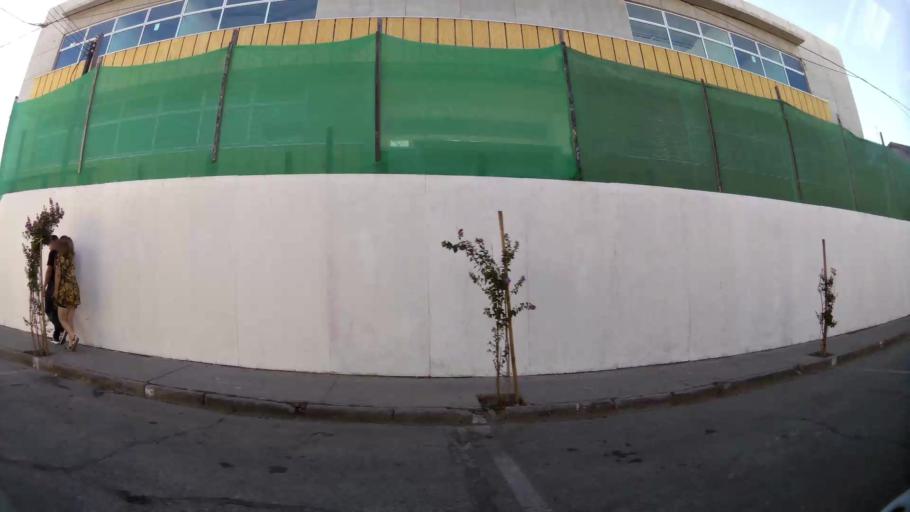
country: CL
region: O'Higgins
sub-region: Provincia de Cachapoal
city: Rancagua
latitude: -34.1717
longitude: -70.7439
